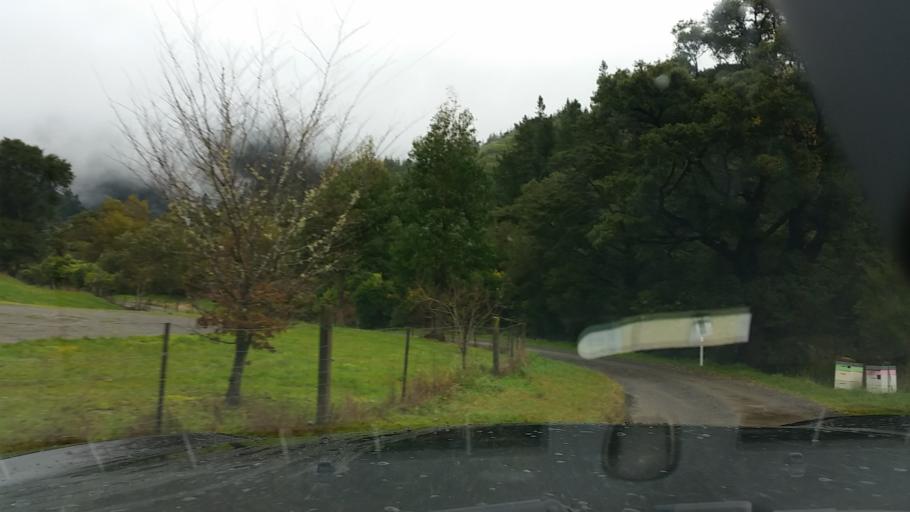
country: NZ
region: Marlborough
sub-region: Marlborough District
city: Picton
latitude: -41.2887
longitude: 174.0392
